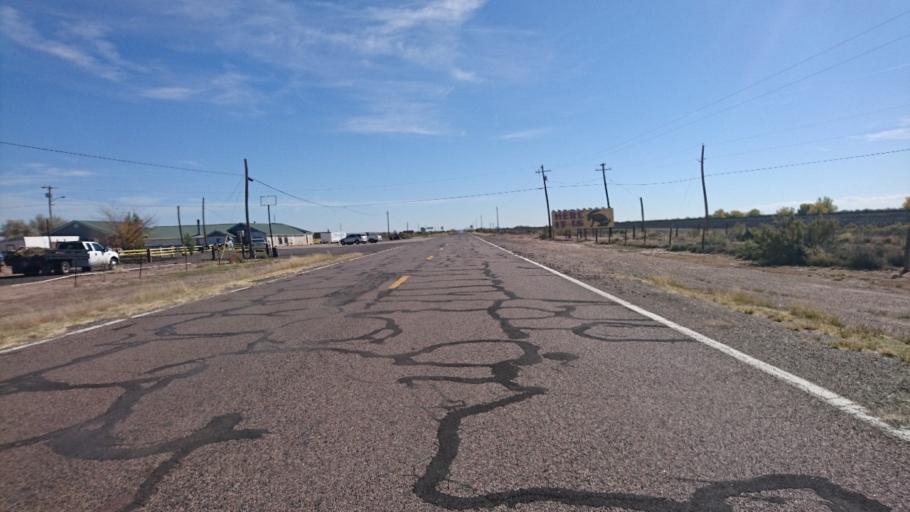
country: US
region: Arizona
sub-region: Navajo County
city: Joseph City
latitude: 34.9679
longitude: -110.4317
